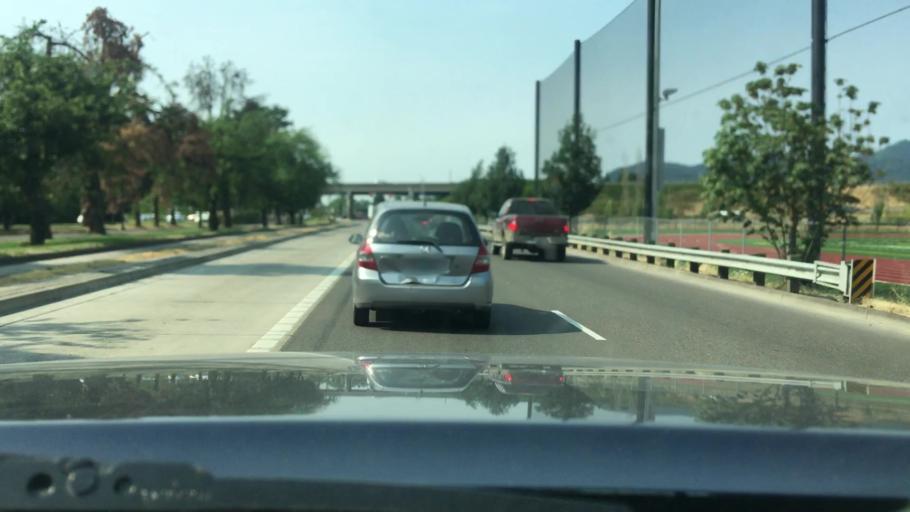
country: US
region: Oregon
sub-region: Lane County
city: Springfield
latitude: 44.0589
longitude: -123.0246
